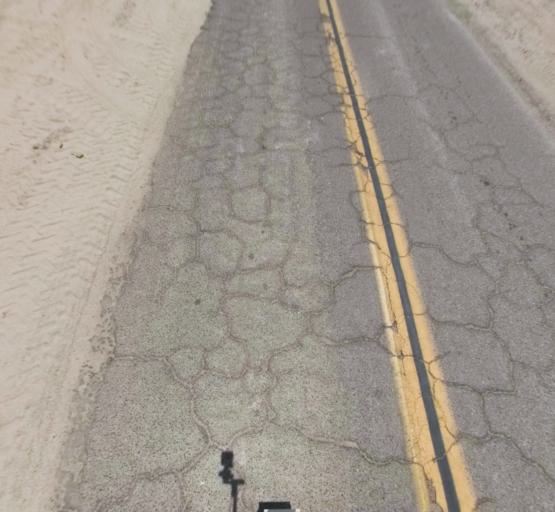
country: US
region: California
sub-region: Fresno County
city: Kerman
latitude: 36.8226
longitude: -120.1509
